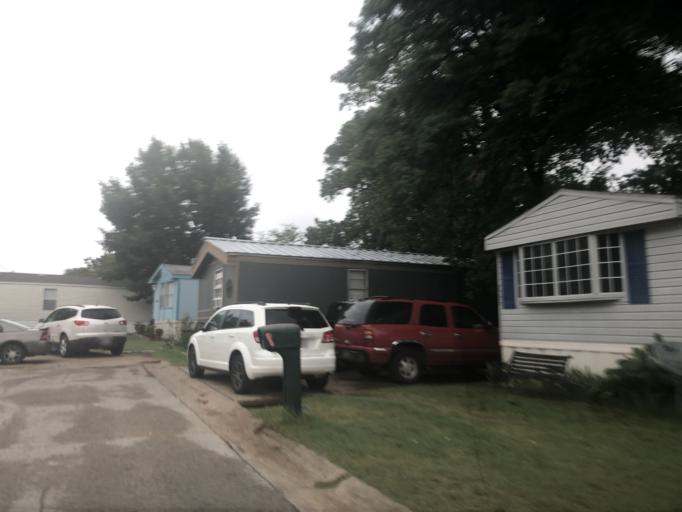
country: US
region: Texas
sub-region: Dallas County
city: Irving
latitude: 32.7929
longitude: -96.9545
